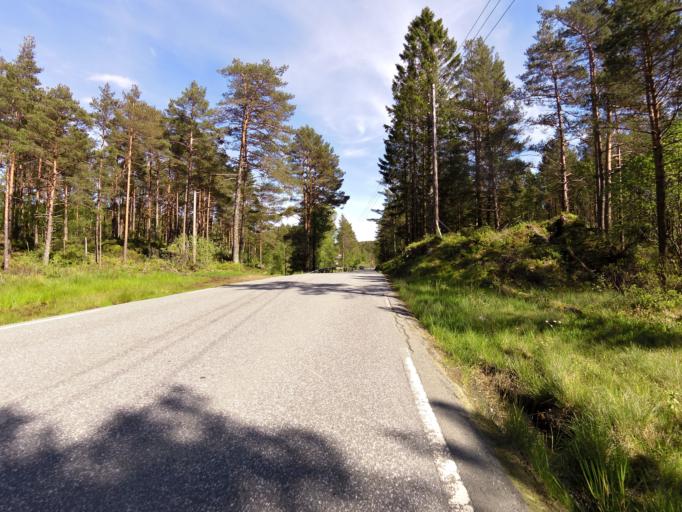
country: NO
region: Hordaland
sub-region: Stord
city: Sagvag
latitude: 59.7886
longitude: 5.4432
